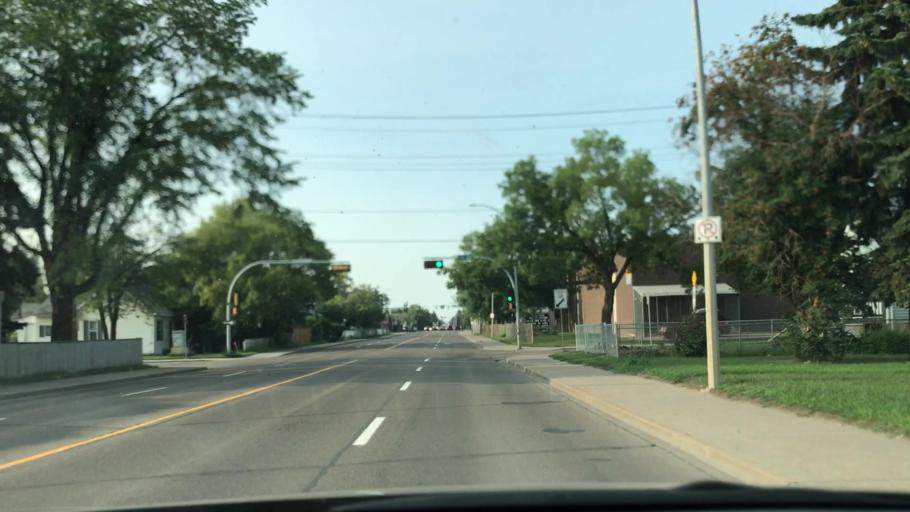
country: CA
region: Alberta
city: Edmonton
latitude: 53.5669
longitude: -113.4673
